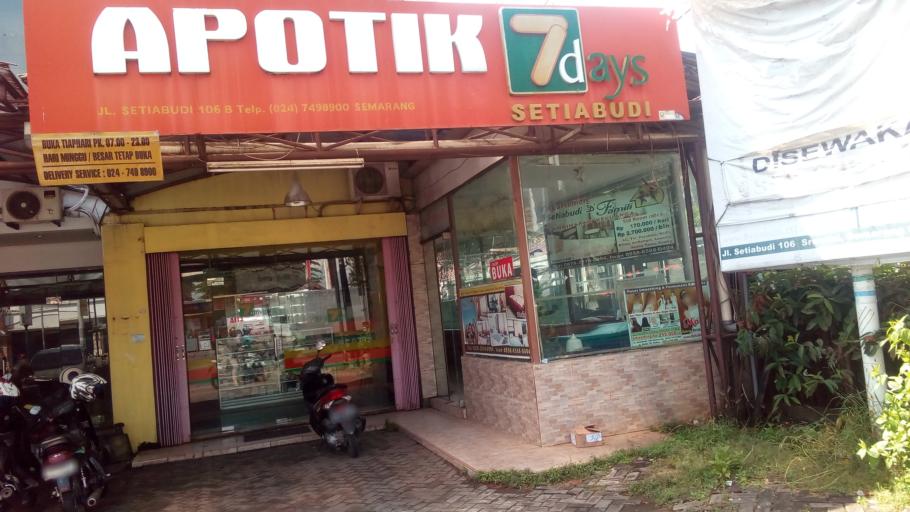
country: ID
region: Central Java
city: Semarang
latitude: -7.0520
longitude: 110.4174
